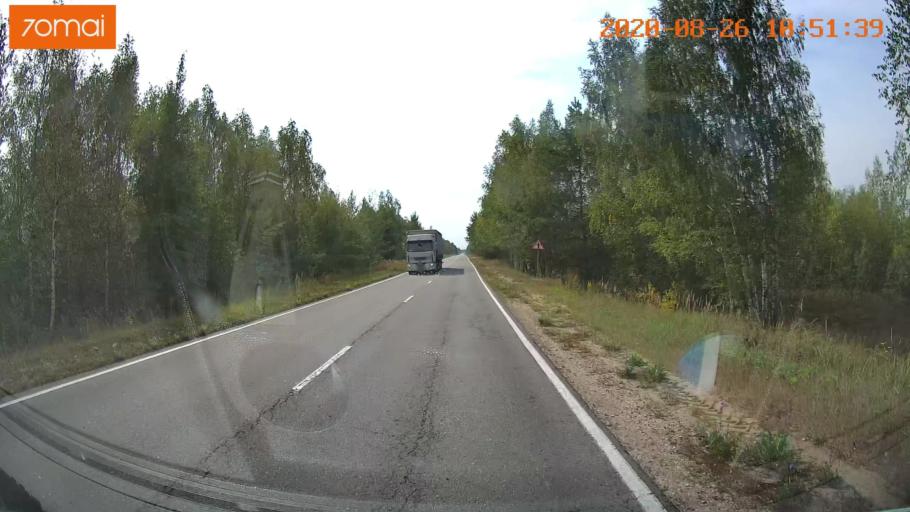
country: RU
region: Rjazan
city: Lashma
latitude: 54.6690
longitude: 41.1547
